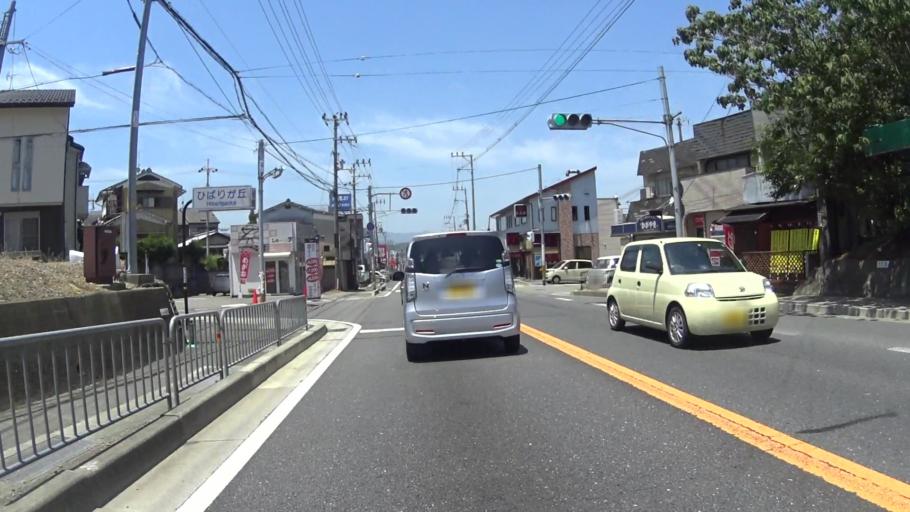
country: JP
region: Kyoto
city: Kameoka
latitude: 35.0027
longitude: 135.5984
